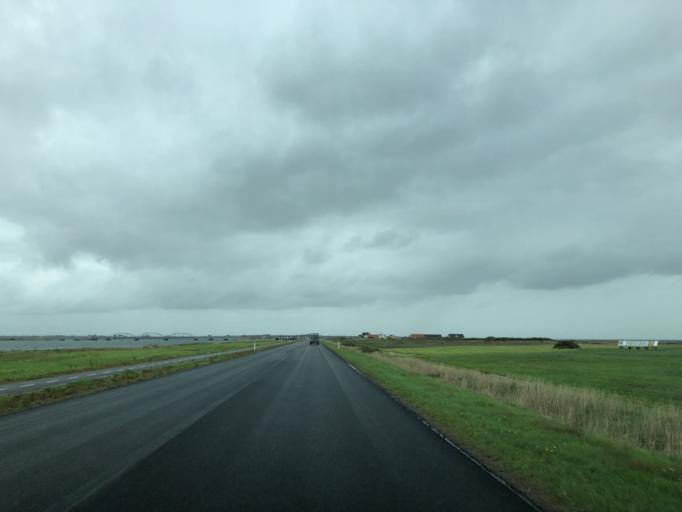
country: DK
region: Central Jutland
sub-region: Struer Kommune
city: Struer
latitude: 56.5657
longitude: 8.5595
